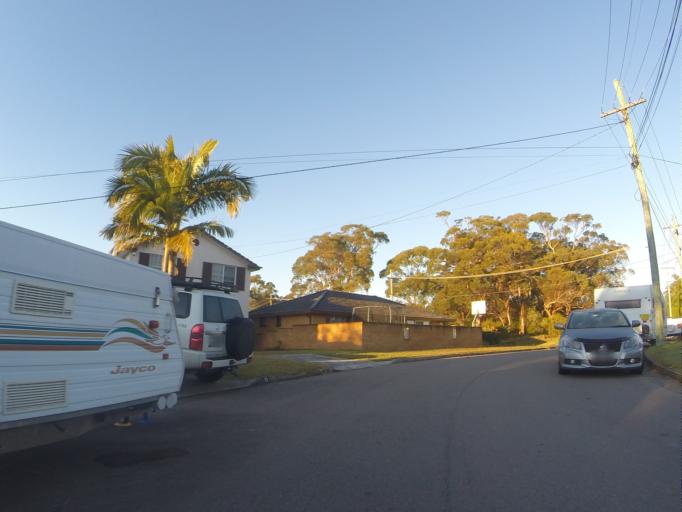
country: AU
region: New South Wales
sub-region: Sutherland Shire
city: Engadine
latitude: -34.0498
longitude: 151.0070
